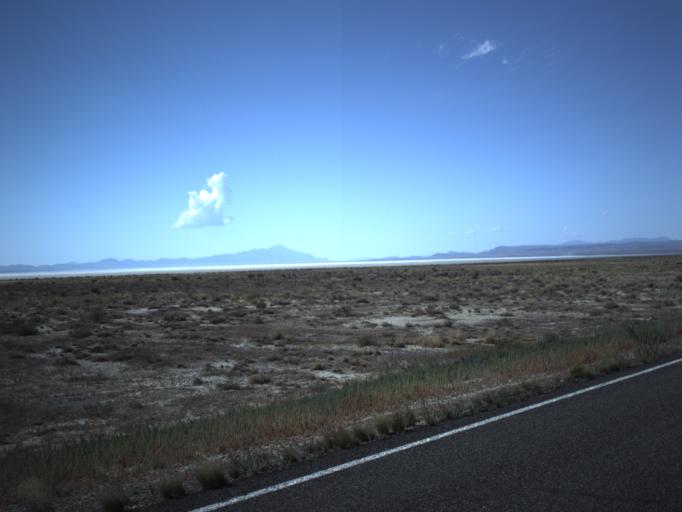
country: US
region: Utah
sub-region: Millard County
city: Delta
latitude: 39.1140
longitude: -113.1313
